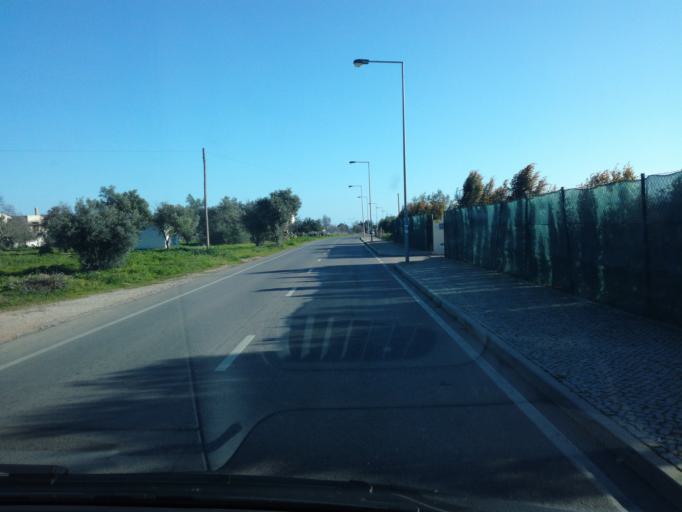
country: PT
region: Faro
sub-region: Olhao
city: Laranjeiro
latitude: 37.0557
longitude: -7.7599
